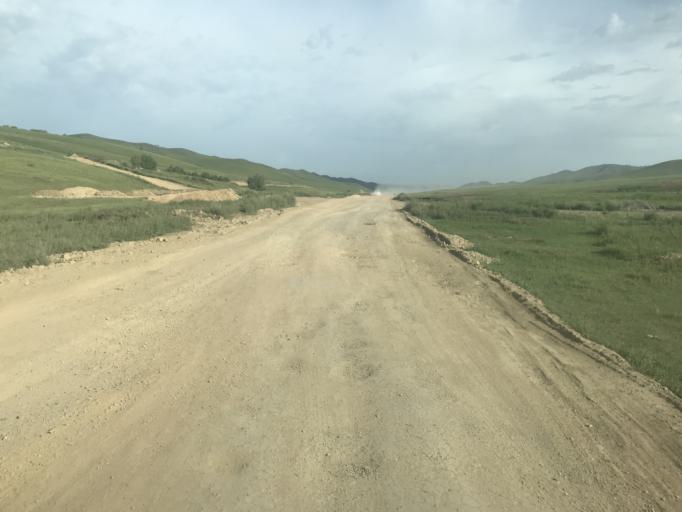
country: MN
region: Central Aimak
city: Javhlant
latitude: 48.7362
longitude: 106.1317
